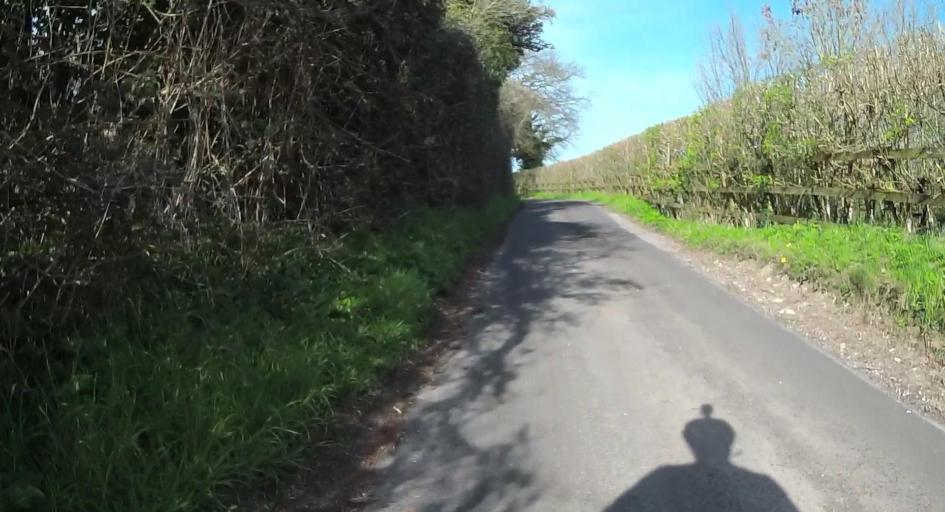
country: GB
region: England
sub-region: Hampshire
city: Highclere
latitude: 51.2682
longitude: -1.3766
